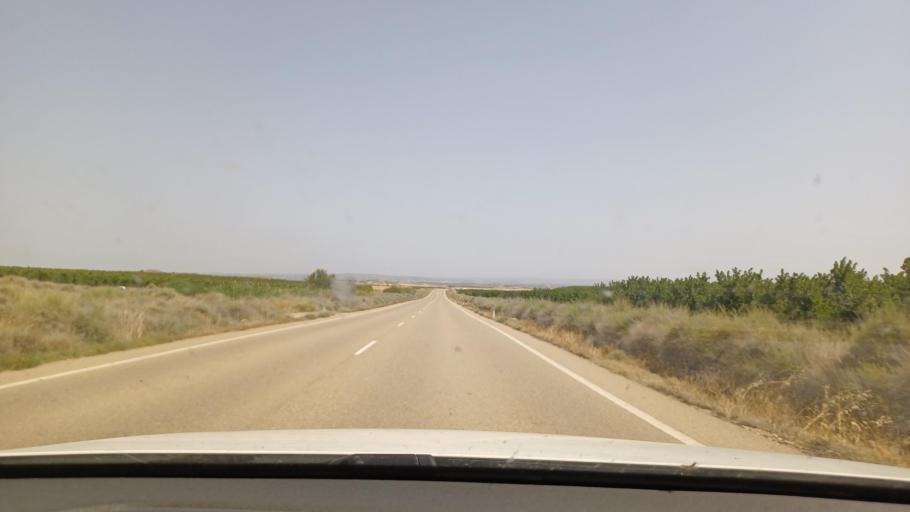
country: ES
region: Aragon
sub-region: Provincia de Zaragoza
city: Chiprana
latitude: 41.3255
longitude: -0.0826
